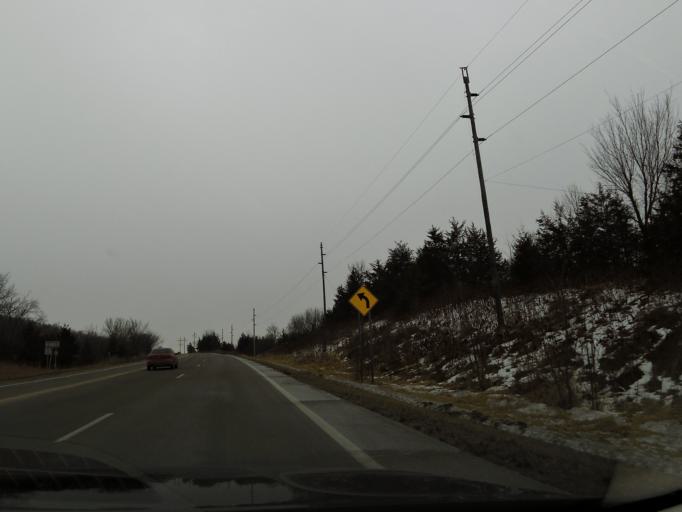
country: US
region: Minnesota
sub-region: Scott County
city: Jordan
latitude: 44.6530
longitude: -93.6285
